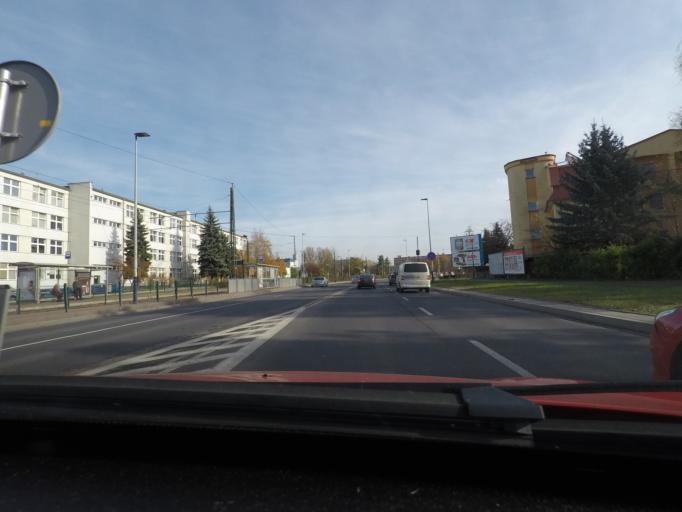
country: PL
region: Lesser Poland Voivodeship
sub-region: Krakow
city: Krakow
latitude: 50.0304
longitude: 19.9315
